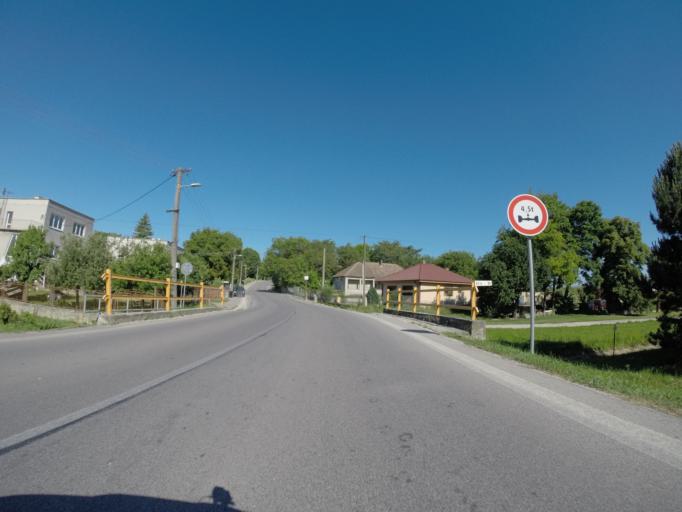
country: SK
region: Nitriansky
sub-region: Okres Nitra
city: Nitra
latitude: 48.5258
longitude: 18.0602
